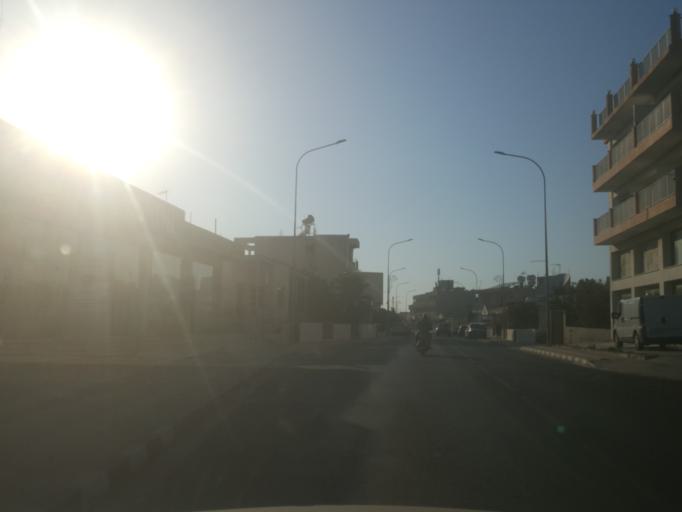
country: CY
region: Ammochostos
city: Deryneia
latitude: 35.0614
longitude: 33.9635
